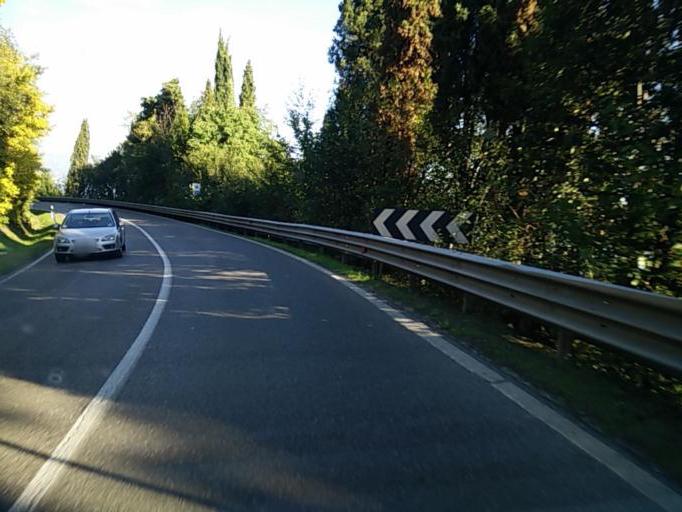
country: IT
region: Lombardy
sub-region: Provincia di Brescia
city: Salo
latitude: 45.6095
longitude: 10.5328
